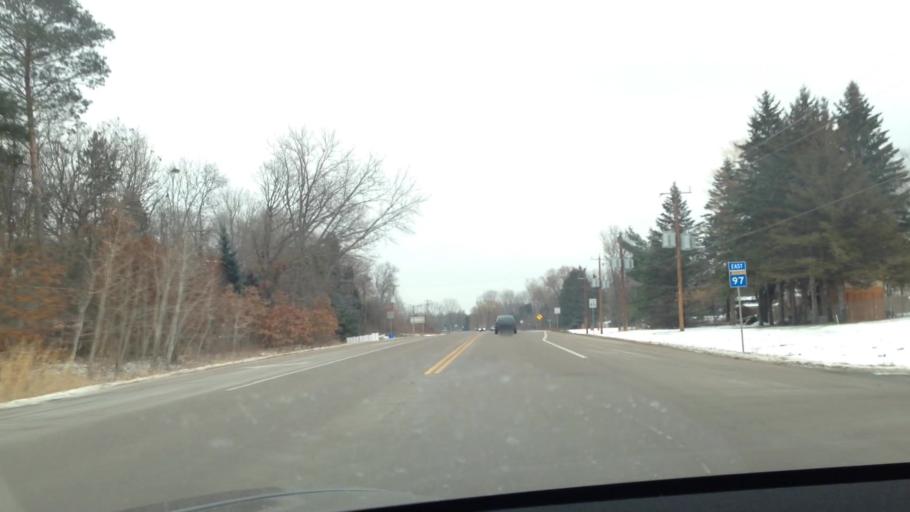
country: US
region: Minnesota
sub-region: Washington County
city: Forest Lake
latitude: 45.2609
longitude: -92.9582
